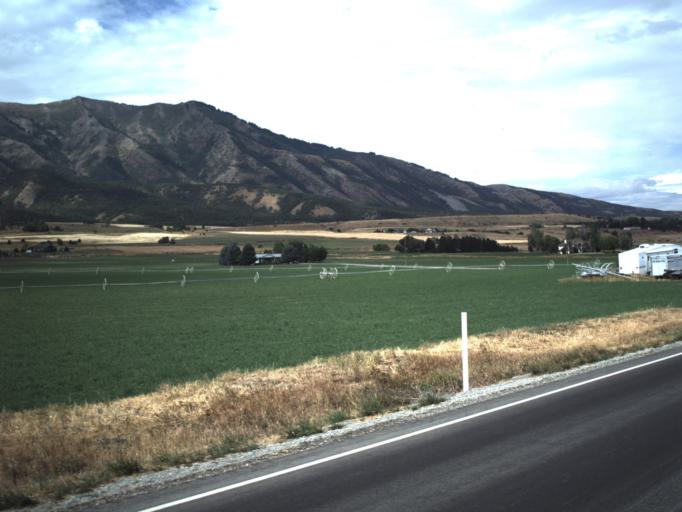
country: US
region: Utah
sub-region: Cache County
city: Mendon
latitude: 41.6763
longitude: -111.9582
